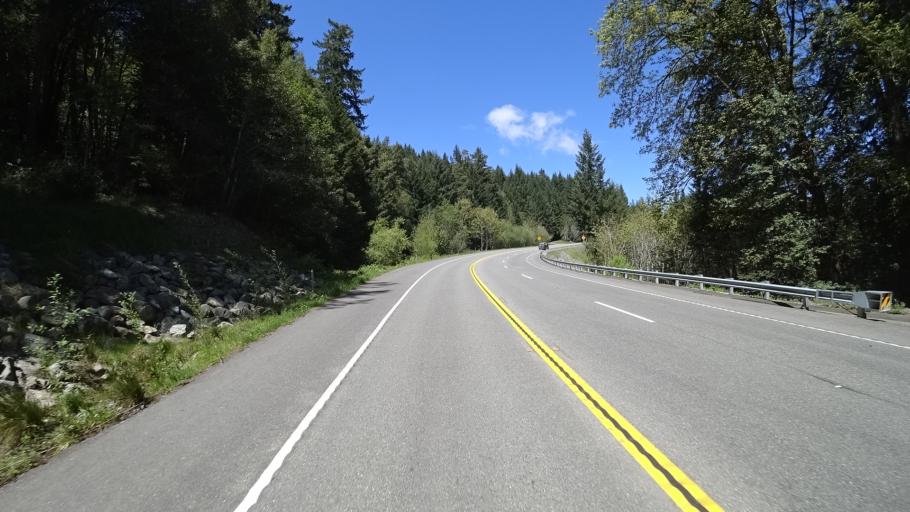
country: US
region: California
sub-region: Humboldt County
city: Blue Lake
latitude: 40.9210
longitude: -123.8363
